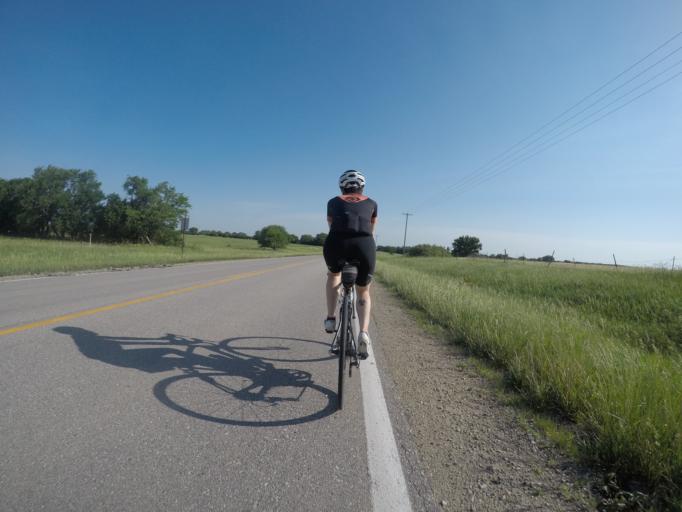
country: US
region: Kansas
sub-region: Riley County
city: Fort Riley North
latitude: 39.3605
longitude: -96.8307
